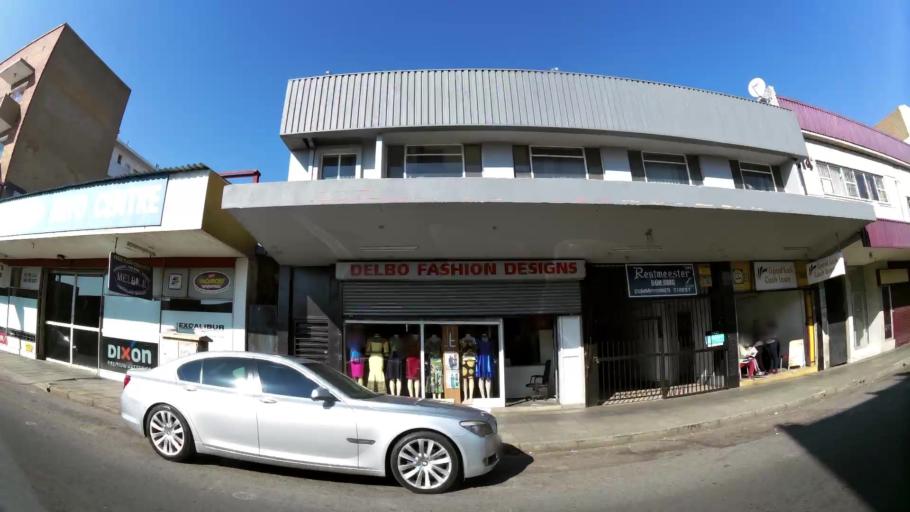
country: ZA
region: Gauteng
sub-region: Ekurhuleni Metropolitan Municipality
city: Boksburg
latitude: -26.2234
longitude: 28.2563
